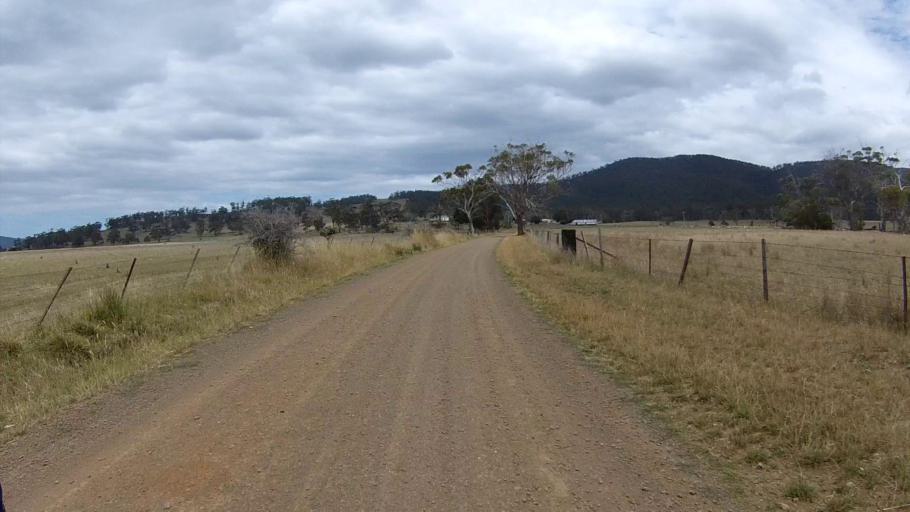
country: AU
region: Tasmania
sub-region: Sorell
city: Sorell
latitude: -42.6563
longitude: 147.9387
